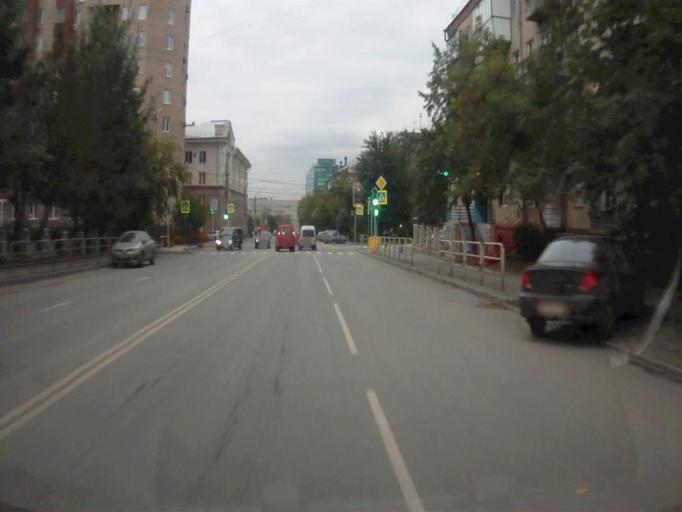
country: RU
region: Chelyabinsk
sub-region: Gorod Chelyabinsk
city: Chelyabinsk
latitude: 55.1548
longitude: 61.3988
